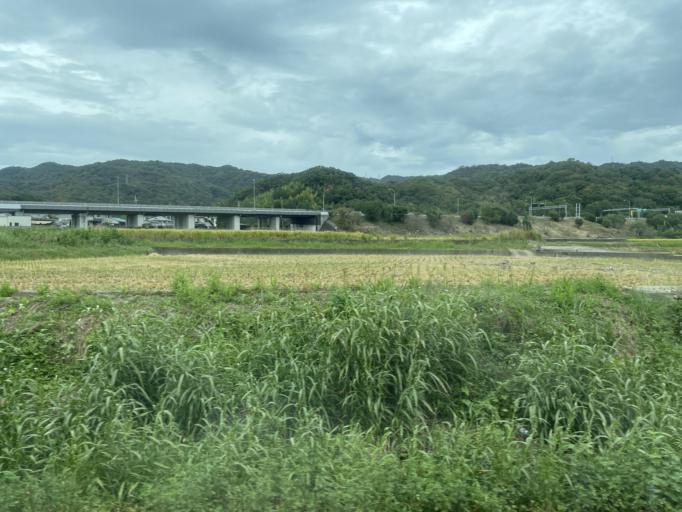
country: JP
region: Wakayama
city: Wakayama-shi
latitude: 34.2685
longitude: 135.2342
